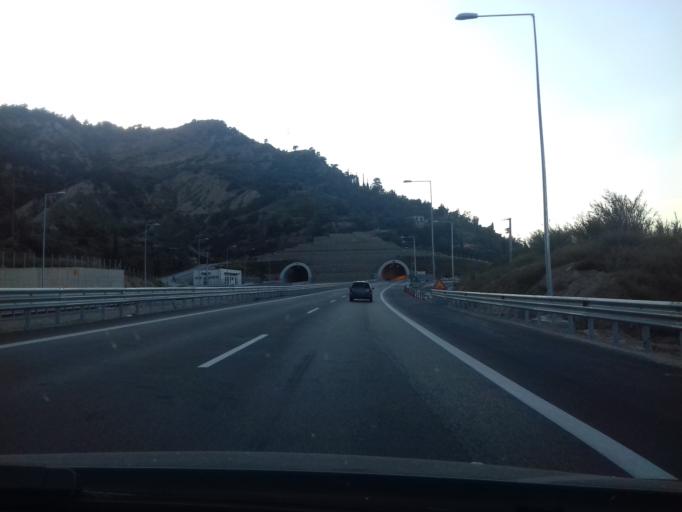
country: GR
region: West Greece
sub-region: Nomos Achaias
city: Aiyira
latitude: 38.1342
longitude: 22.3917
